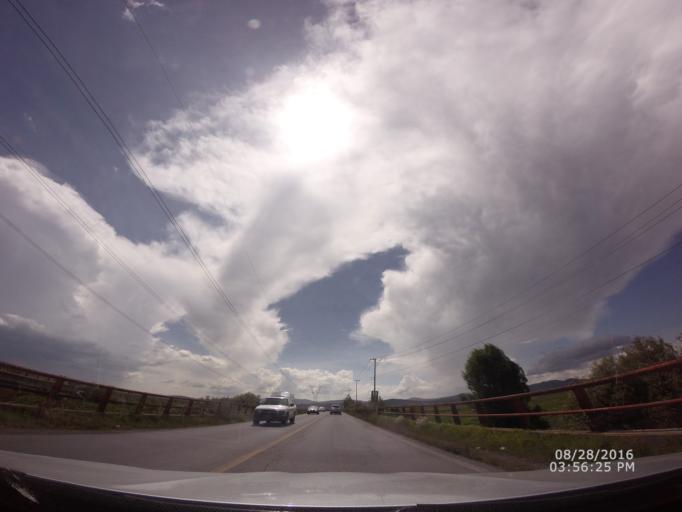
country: MX
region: Hidalgo
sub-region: Mineral de la Reforma
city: Los Tuzos
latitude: 20.0360
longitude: -98.7557
